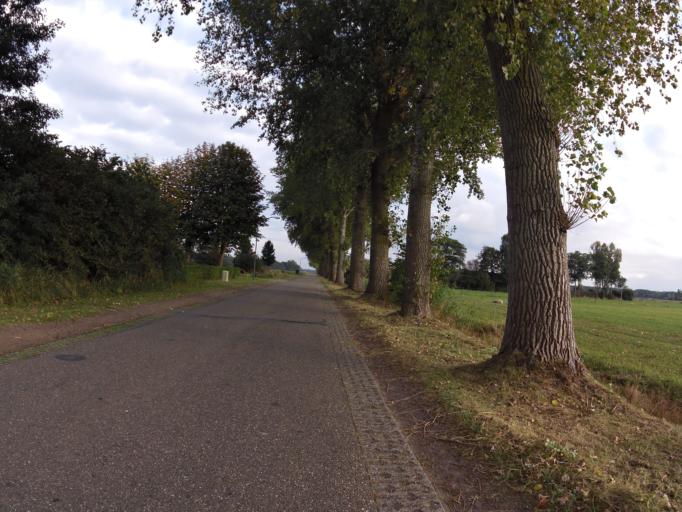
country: NL
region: North Brabant
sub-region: Gemeente Vught
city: Vught
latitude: 51.6826
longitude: 5.2347
